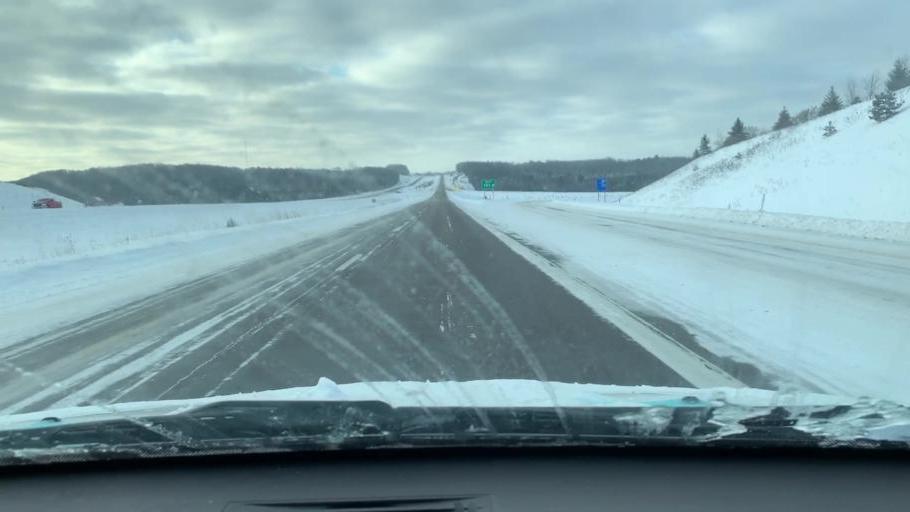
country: US
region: Michigan
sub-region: Wexford County
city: Manton
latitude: 44.4094
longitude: -85.3812
